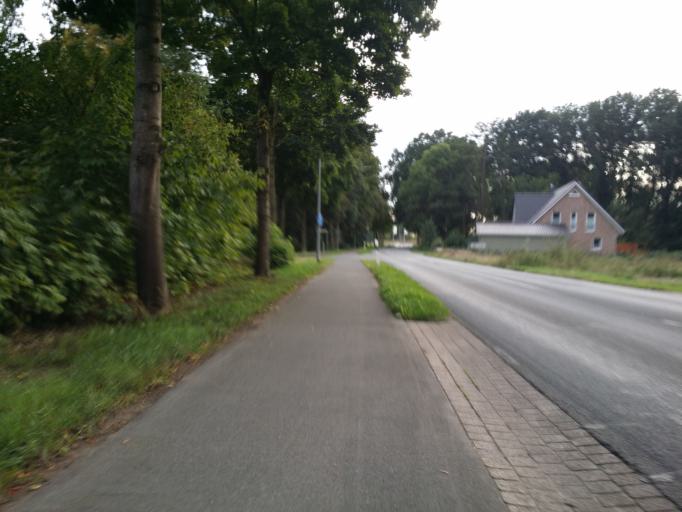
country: DE
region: Lower Saxony
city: Bremervorde
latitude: 53.4717
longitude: 9.1320
